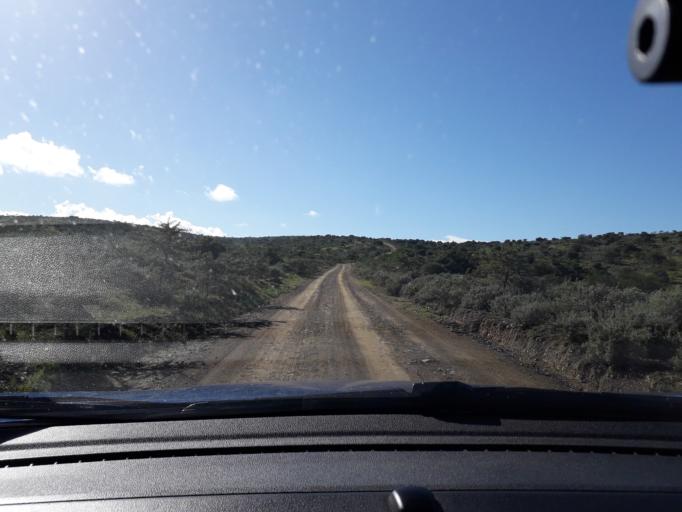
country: ZA
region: Eastern Cape
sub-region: Buffalo City Metropolitan Municipality
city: Bhisho
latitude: -33.1217
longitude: 27.4524
